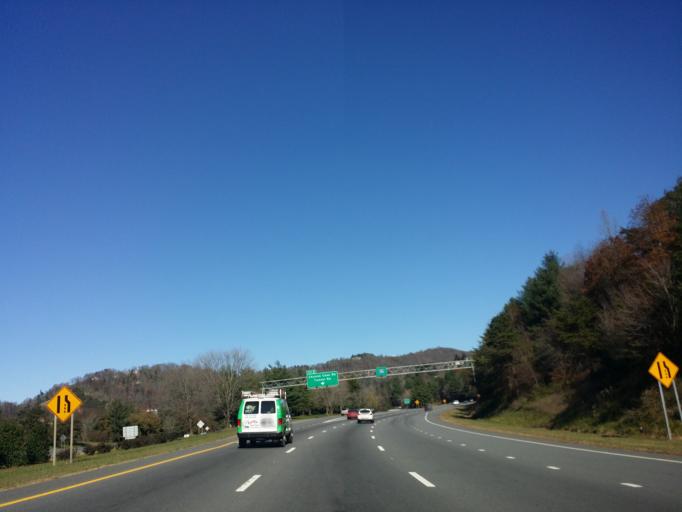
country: US
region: North Carolina
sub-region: Buncombe County
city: Asheville
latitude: 35.5905
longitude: -82.5271
